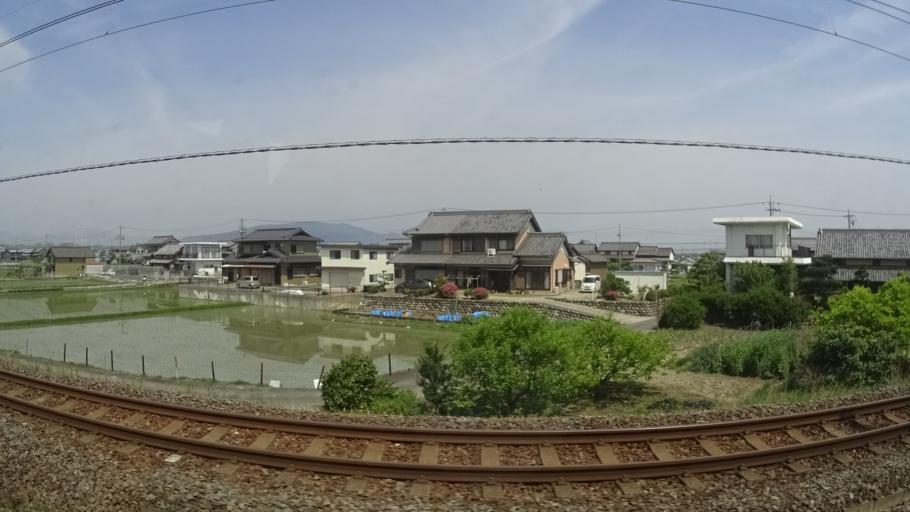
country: JP
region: Aichi
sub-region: Tsushima-shi
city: Tsushima
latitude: 35.0975
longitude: 136.6940
